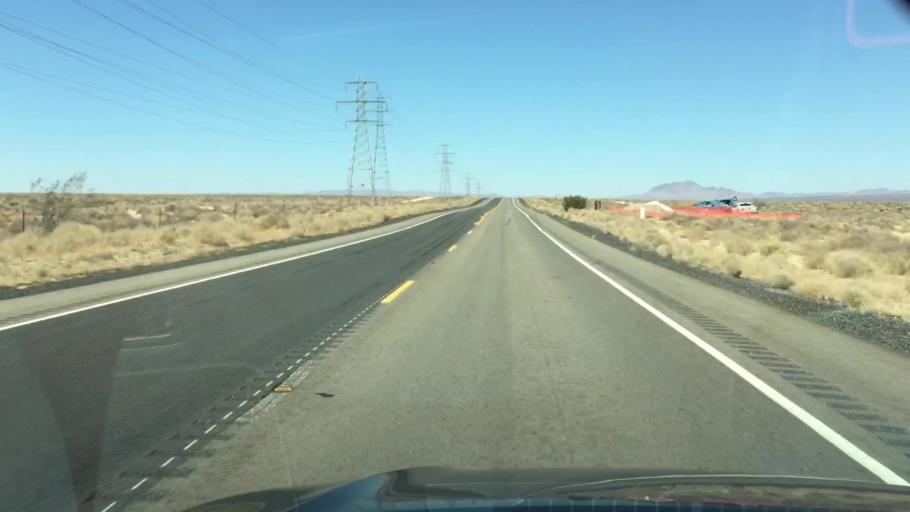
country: US
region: California
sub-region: Kern County
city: Boron
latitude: 35.1027
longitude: -117.5723
